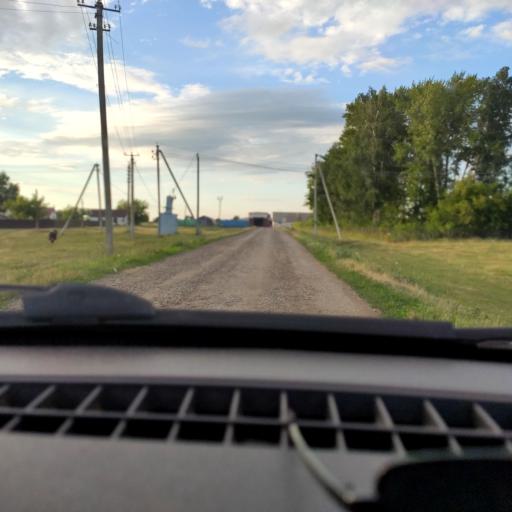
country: RU
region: Bashkortostan
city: Chishmy
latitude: 54.3755
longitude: 55.4209
